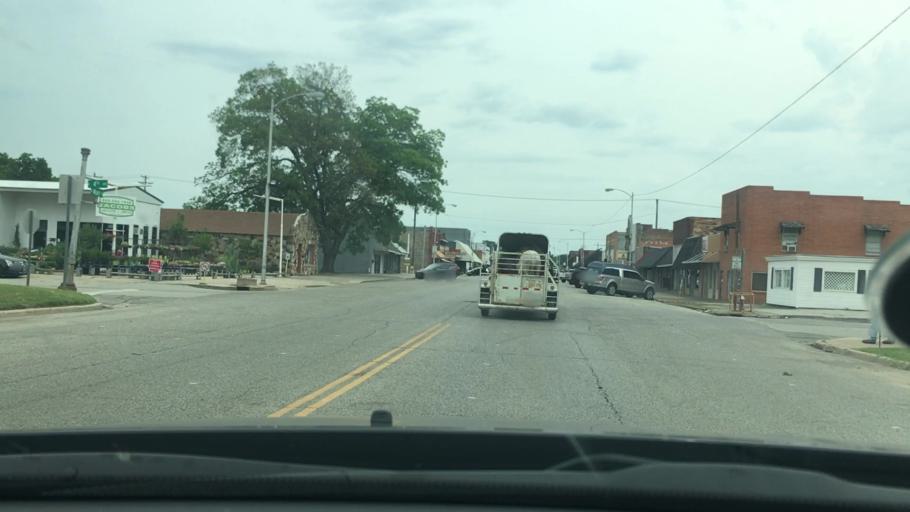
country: US
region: Oklahoma
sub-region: Love County
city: Marietta
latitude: 33.9374
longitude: -97.1208
